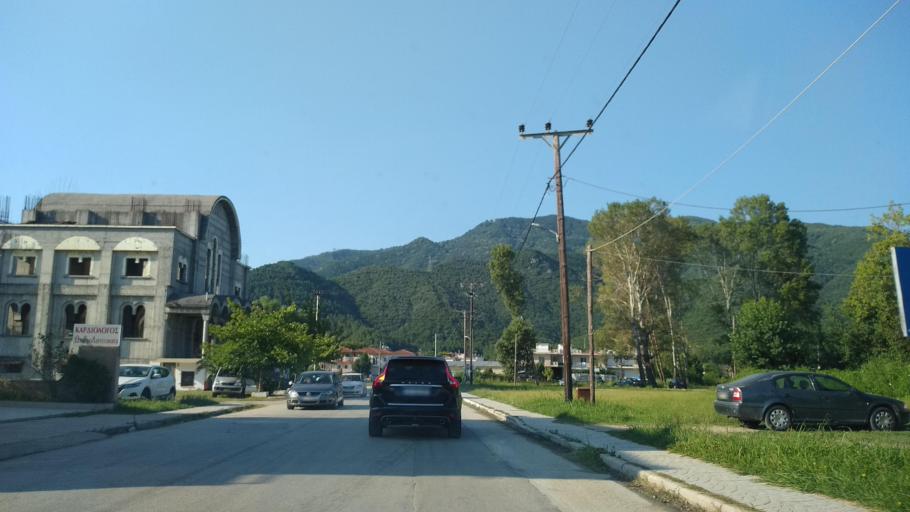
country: GR
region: Central Macedonia
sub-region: Nomos Thessalonikis
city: Stavros
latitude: 40.6674
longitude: 23.6912
